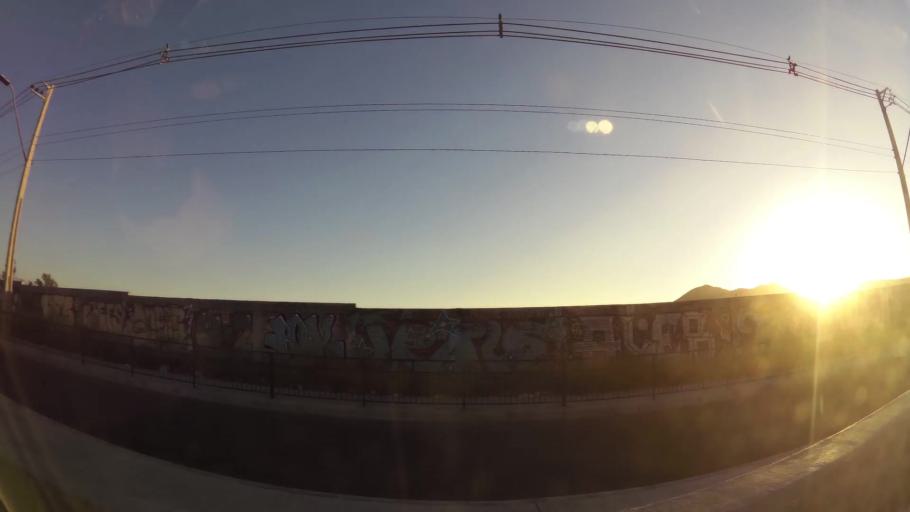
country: CL
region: Santiago Metropolitan
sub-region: Provincia de Maipo
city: San Bernardo
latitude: -33.5748
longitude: -70.6964
